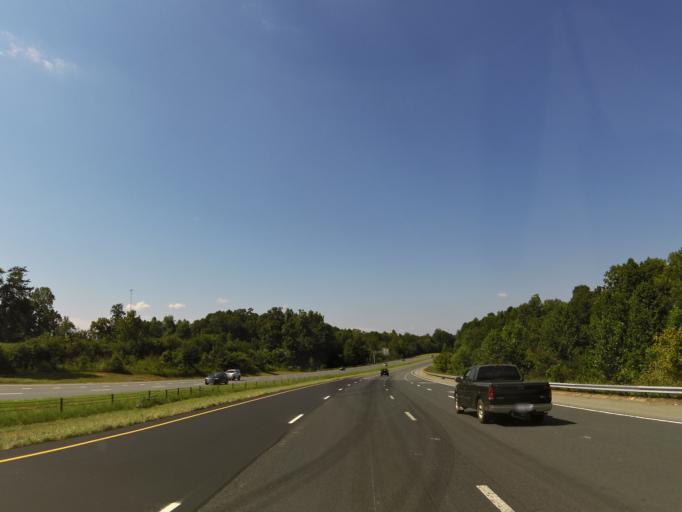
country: US
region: North Carolina
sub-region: Lincoln County
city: Lincolnton
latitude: 35.4825
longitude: -81.2317
